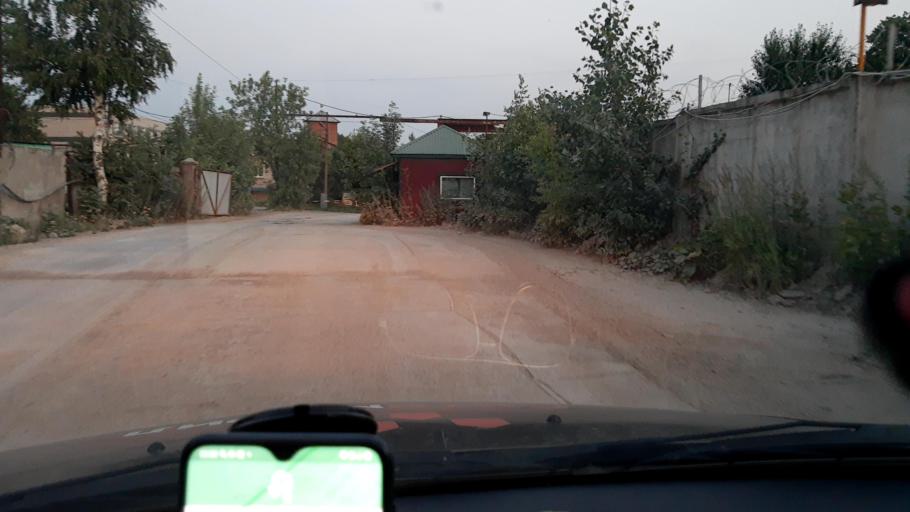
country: RU
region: Bashkortostan
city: Ufa
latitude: 54.8398
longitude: 56.0852
